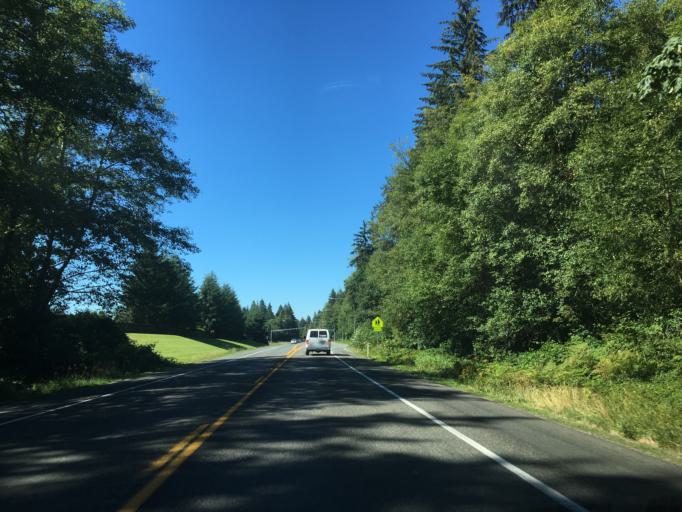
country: US
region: Washington
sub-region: Snohomish County
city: Arlington
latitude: 48.1619
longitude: -122.1176
